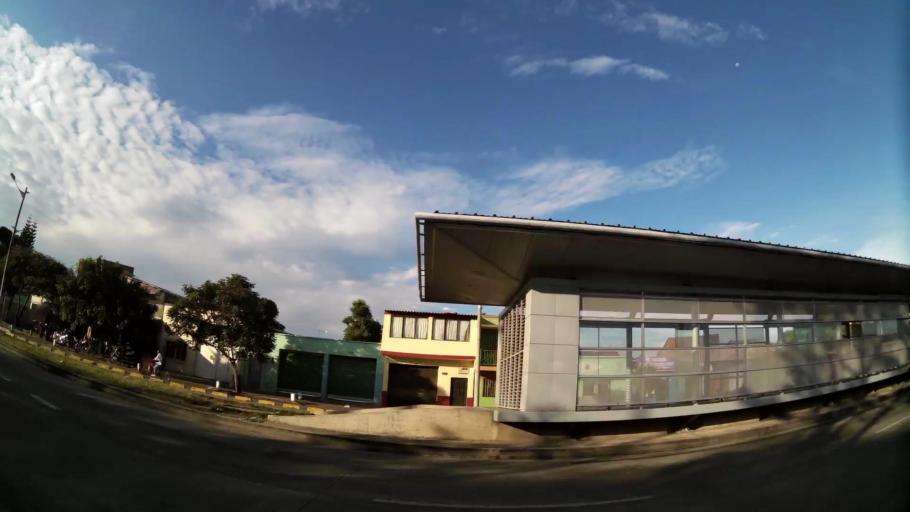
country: CO
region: Valle del Cauca
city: Cali
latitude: 3.4322
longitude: -76.5105
